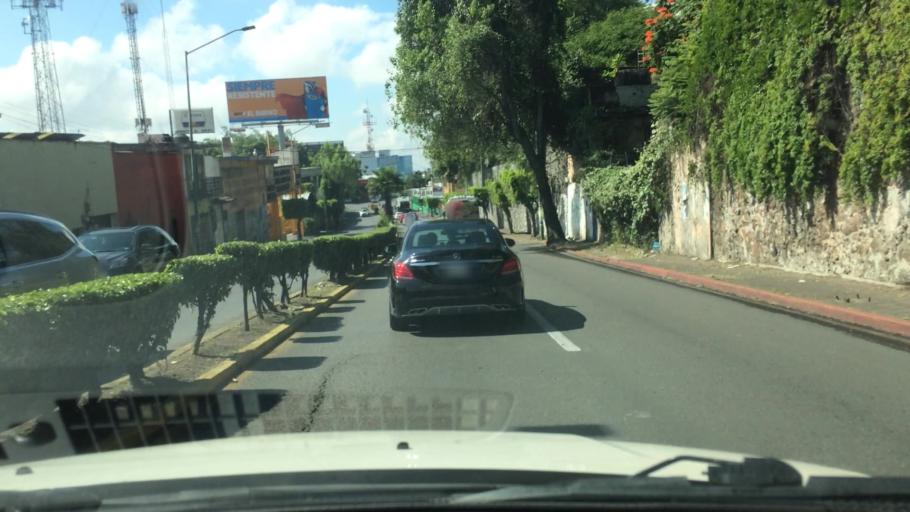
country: MX
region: Morelos
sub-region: Cuernavaca
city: Fraccionamiento Lomas de Ahuatlan
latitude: 18.9446
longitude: -99.2430
